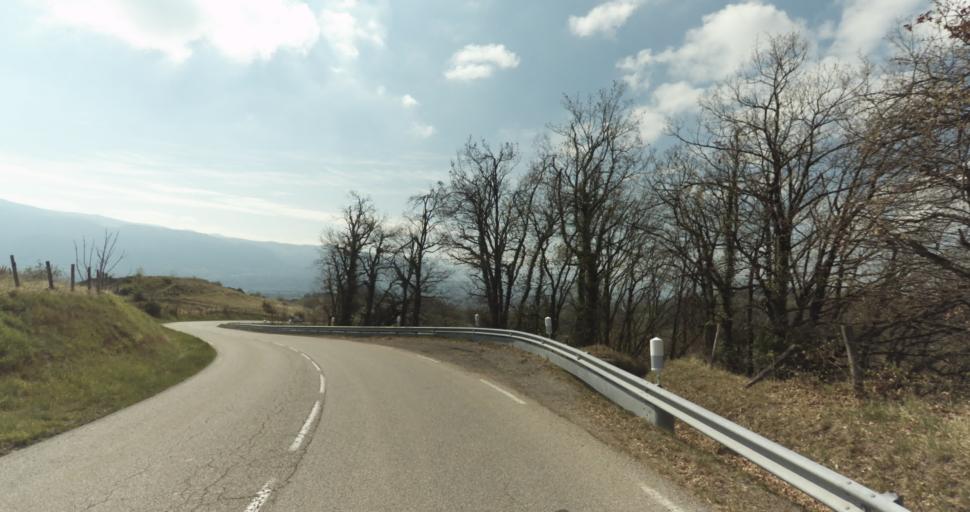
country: FR
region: Rhone-Alpes
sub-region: Departement de l'Isere
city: Saint-Verand
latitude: 45.1749
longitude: 5.3169
